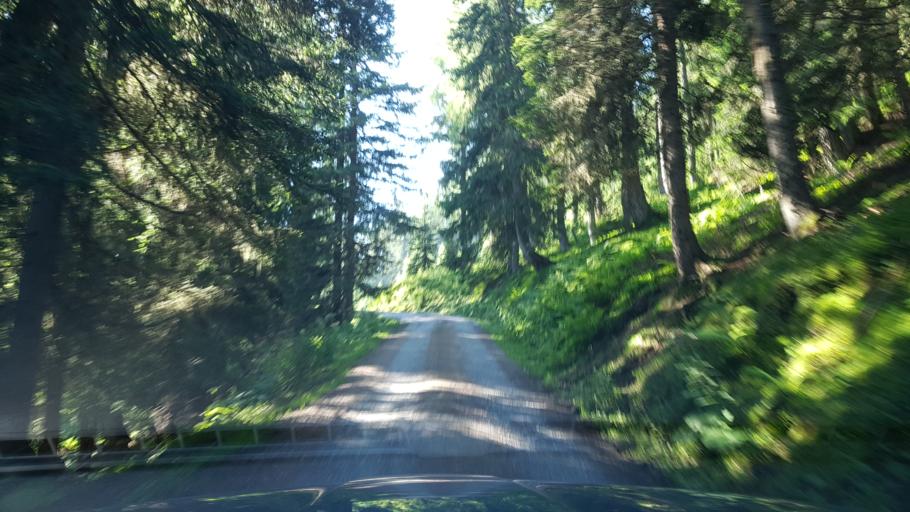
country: AT
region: Salzburg
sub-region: Politischer Bezirk Sankt Johann im Pongau
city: Dorfgastein
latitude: 47.2423
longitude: 13.0695
